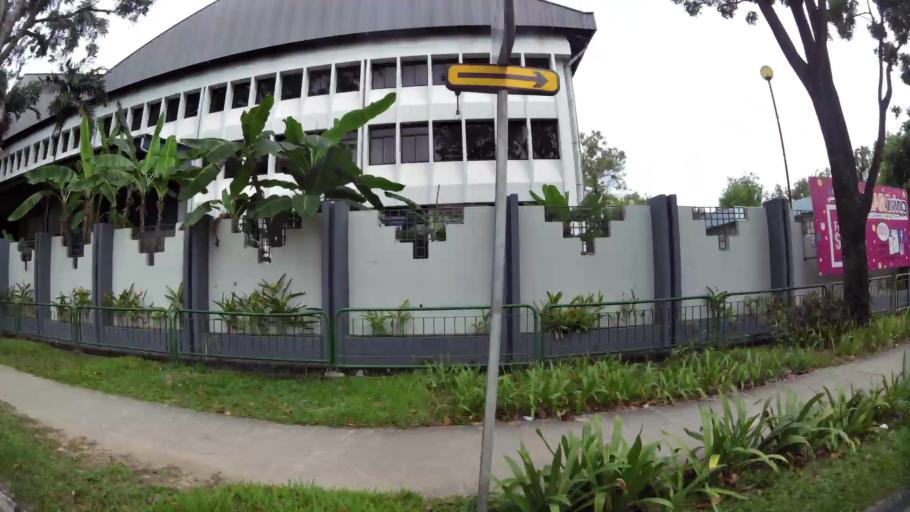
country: MY
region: Johor
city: Johor Bahru
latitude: 1.4083
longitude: 103.7465
